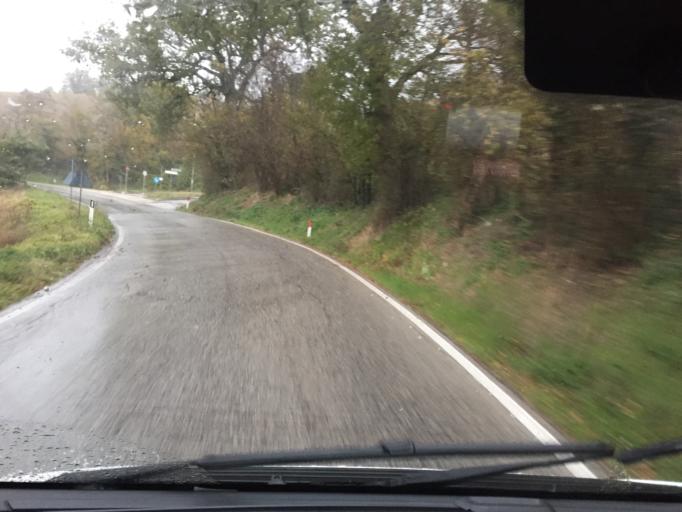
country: IT
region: The Marches
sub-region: Provincia di Macerata
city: Camerino
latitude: 43.1256
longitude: 13.0640
